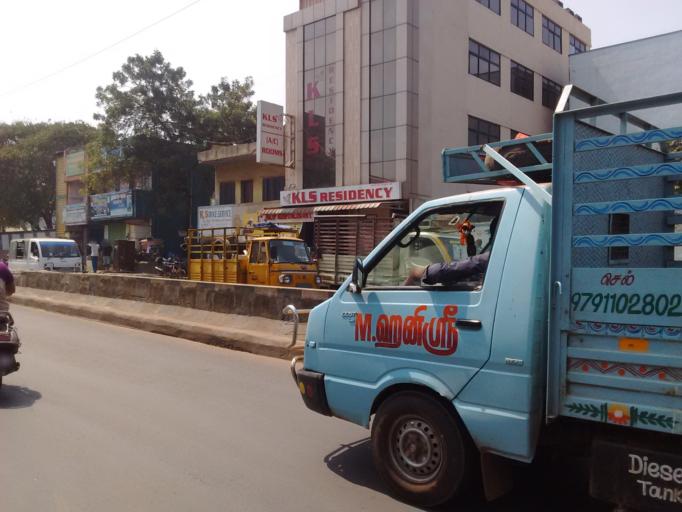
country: IN
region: Tamil Nadu
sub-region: Thiruvallur
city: Tiruvottiyur
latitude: 13.1748
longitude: 80.3061
